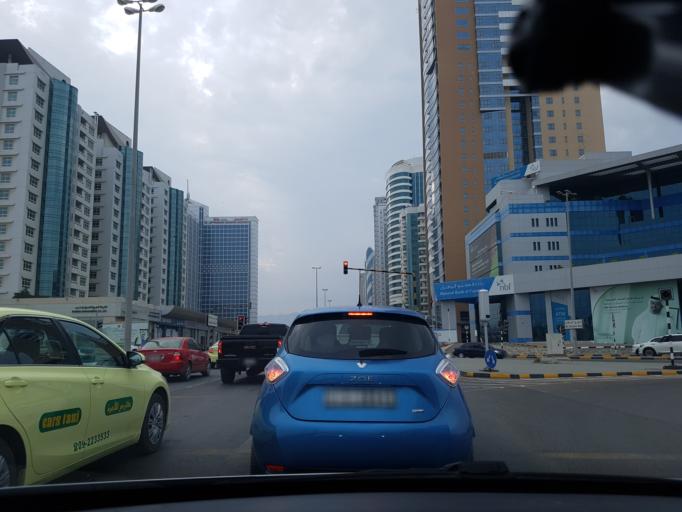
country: AE
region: Al Fujayrah
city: Al Fujayrah
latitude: 25.1222
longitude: 56.3285
